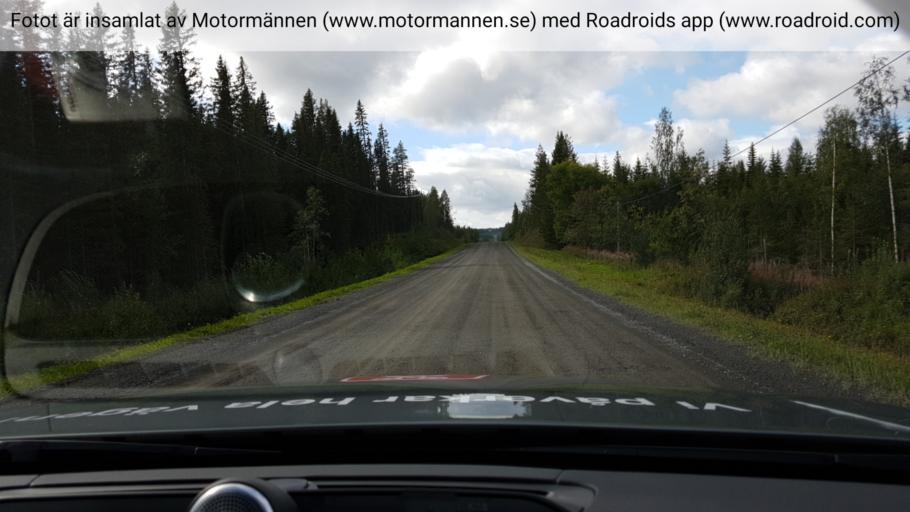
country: SE
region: Jaemtland
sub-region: Stroemsunds Kommun
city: Stroemsund
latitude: 63.6233
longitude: 15.1648
